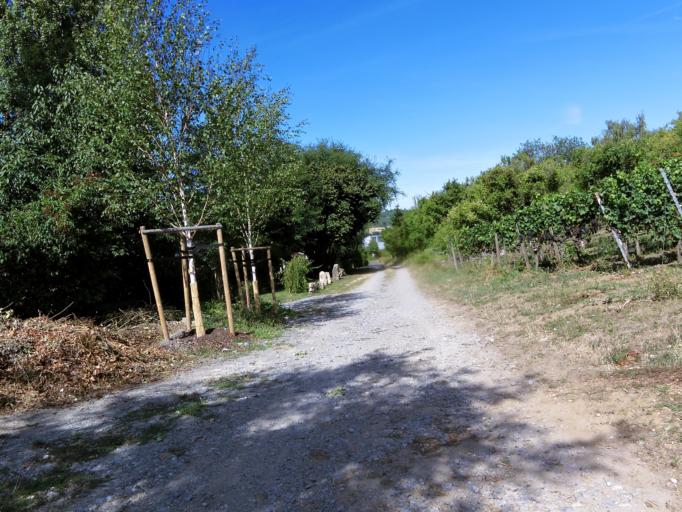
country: DE
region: Bavaria
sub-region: Regierungsbezirk Unterfranken
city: Randersacker
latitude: 49.7448
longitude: 9.9935
